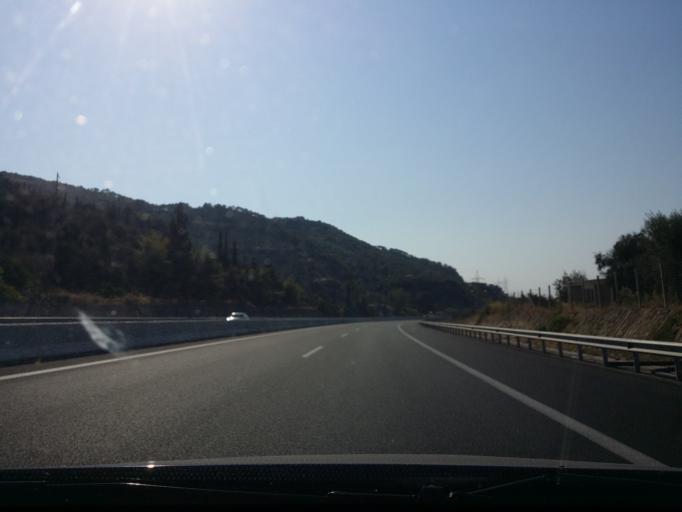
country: GR
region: West Greece
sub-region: Nomos Achaias
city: Aiyira
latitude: 38.1259
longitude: 22.4560
